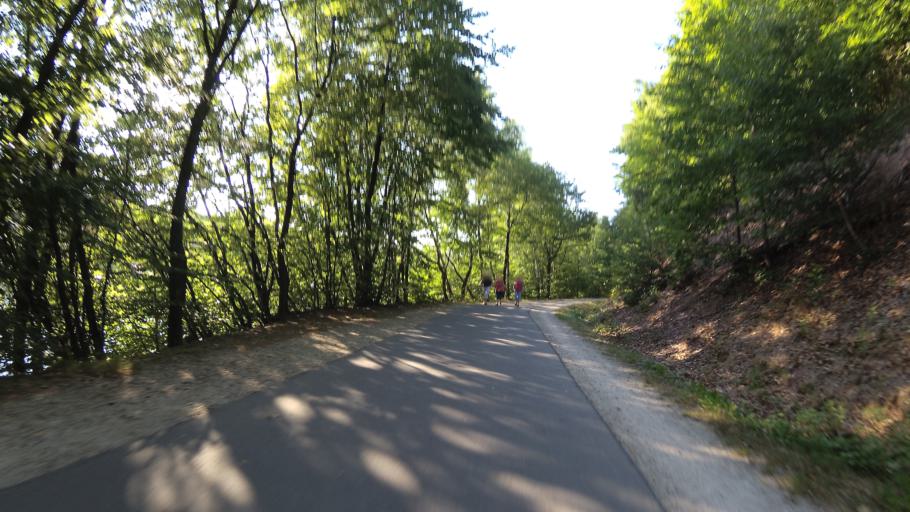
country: DE
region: Rheinland-Pfalz
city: Achtelsbach
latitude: 49.5724
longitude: 7.0685
